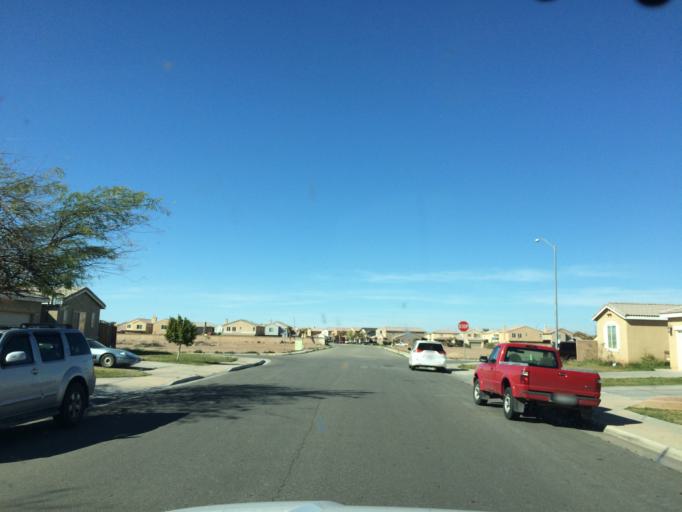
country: US
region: California
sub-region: Imperial County
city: Heber
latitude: 32.7373
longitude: -115.5364
